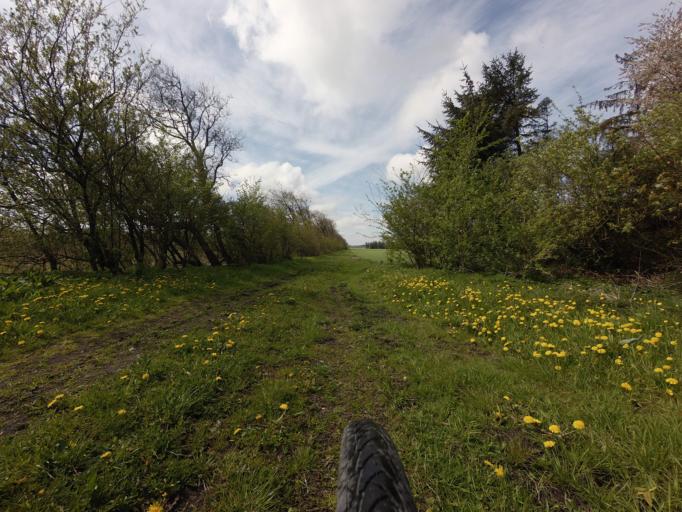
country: DK
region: North Denmark
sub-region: Jammerbugt Kommune
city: Kas
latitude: 57.1985
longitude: 9.6235
